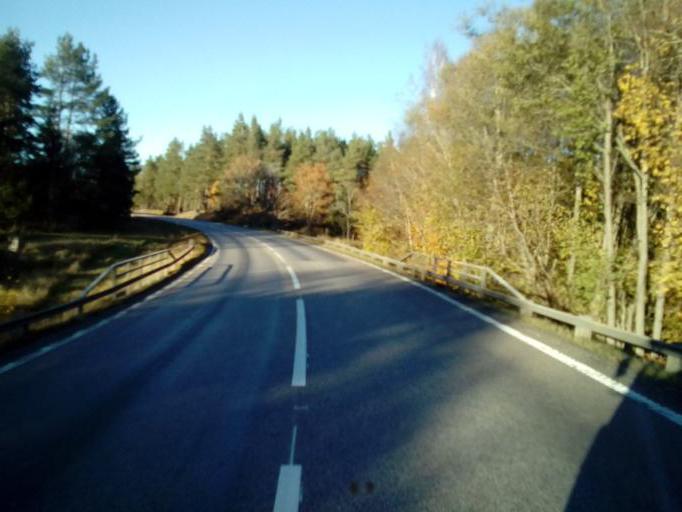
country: SE
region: OErebro
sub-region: Hallsbergs Kommun
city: Palsboda
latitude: 58.8626
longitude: 15.4125
